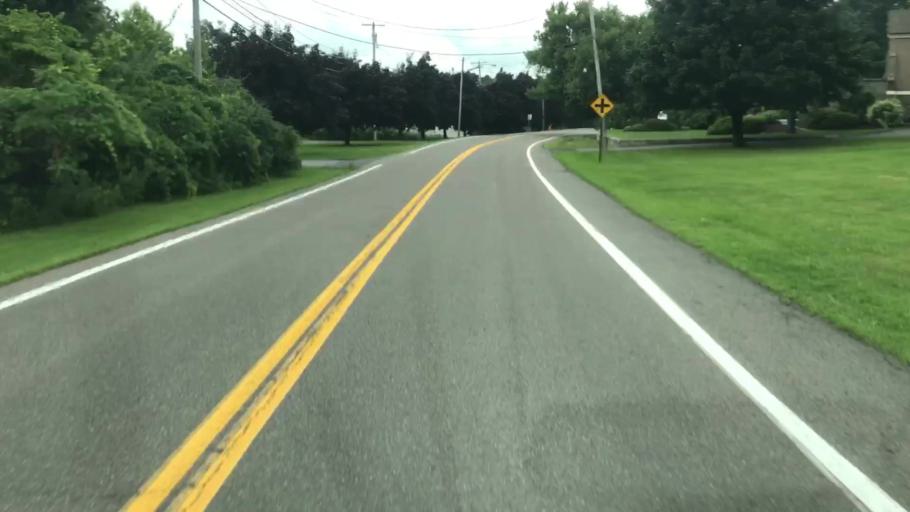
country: US
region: New York
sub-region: Onondaga County
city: Elbridge
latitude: 42.9930
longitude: -76.4564
